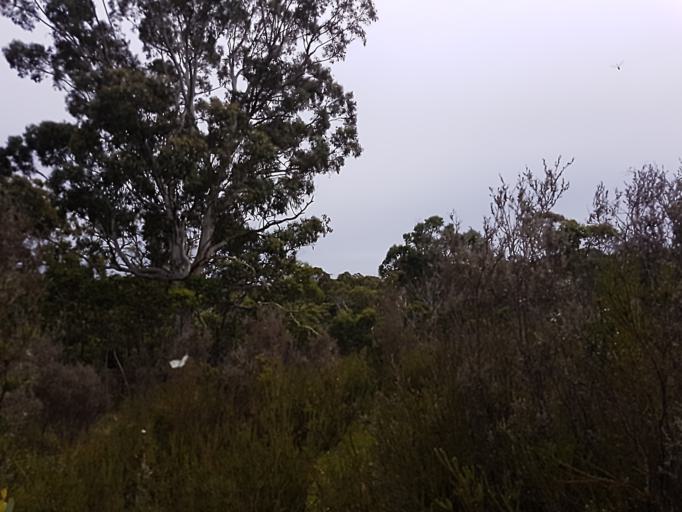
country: AU
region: New South Wales
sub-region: Snowy River
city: Jindabyne
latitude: -36.8039
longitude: 148.1872
